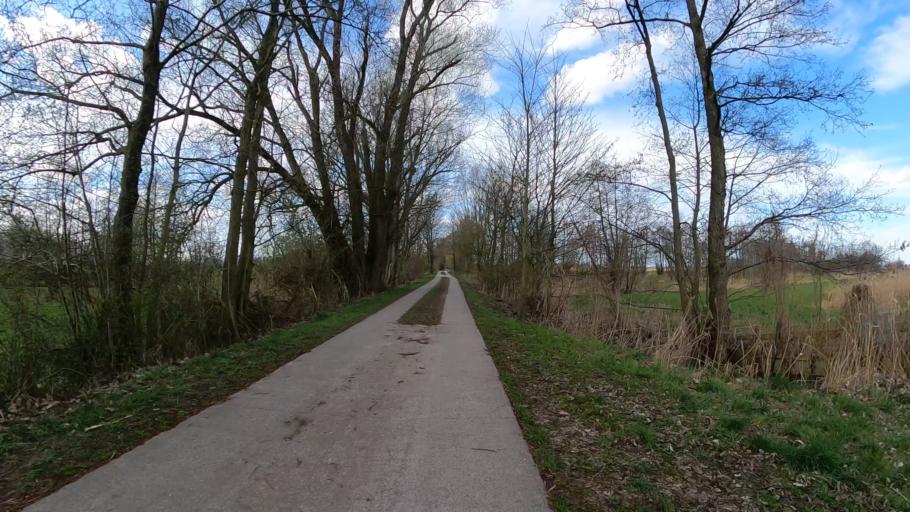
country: DE
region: Lower Saxony
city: Stelle
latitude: 53.4207
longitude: 10.1719
